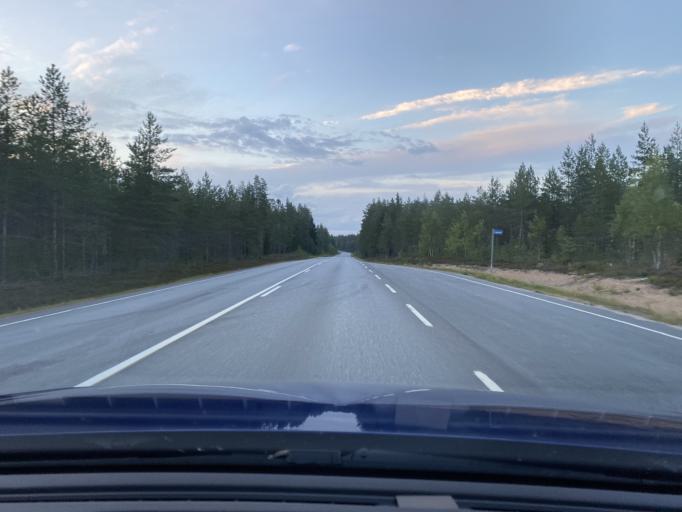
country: FI
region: Satakunta
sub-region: Pohjois-Satakunta
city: Honkajoki
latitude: 62.0323
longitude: 22.2368
